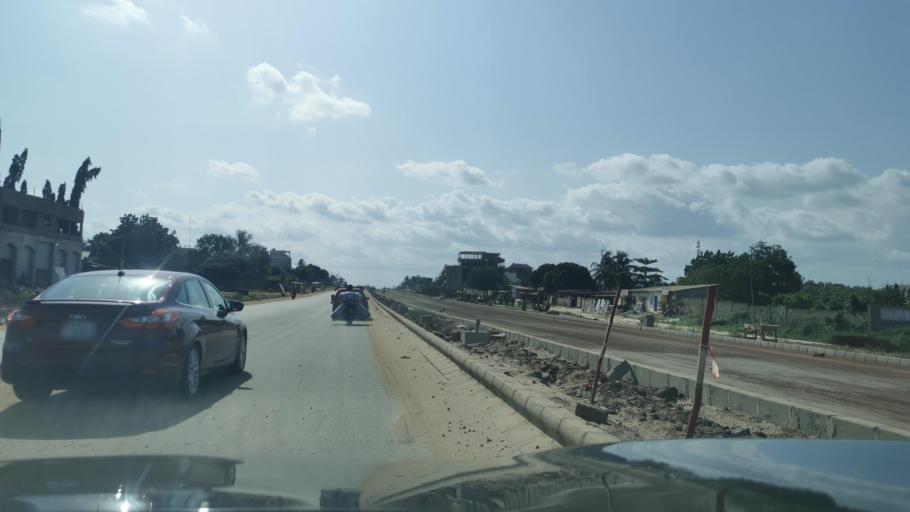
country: TG
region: Maritime
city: Lome
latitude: 6.2146
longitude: 1.1321
